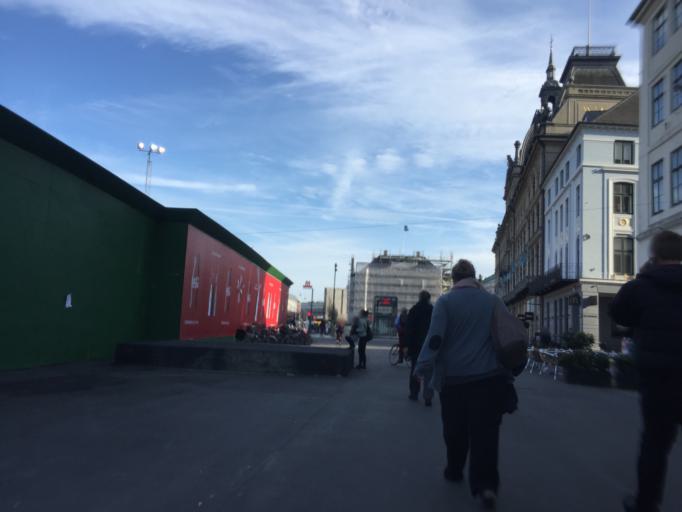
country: DK
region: Capital Region
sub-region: Kobenhavn
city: Christianshavn
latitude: 55.6801
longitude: 12.5849
